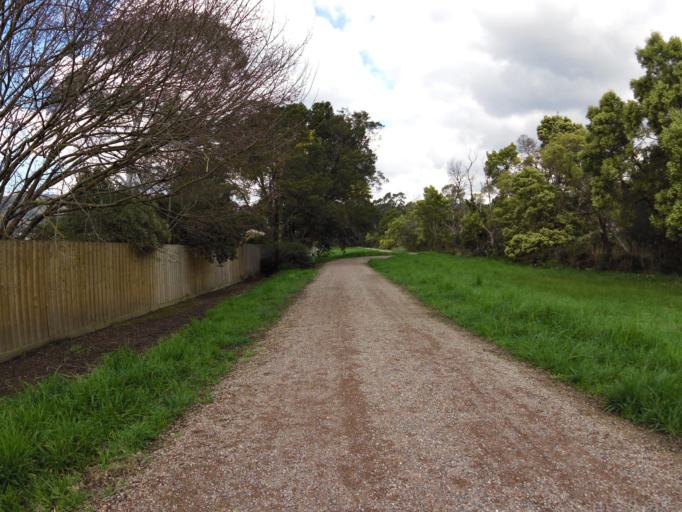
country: AU
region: Victoria
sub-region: Knox
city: The Basin
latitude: -37.8399
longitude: 145.3058
